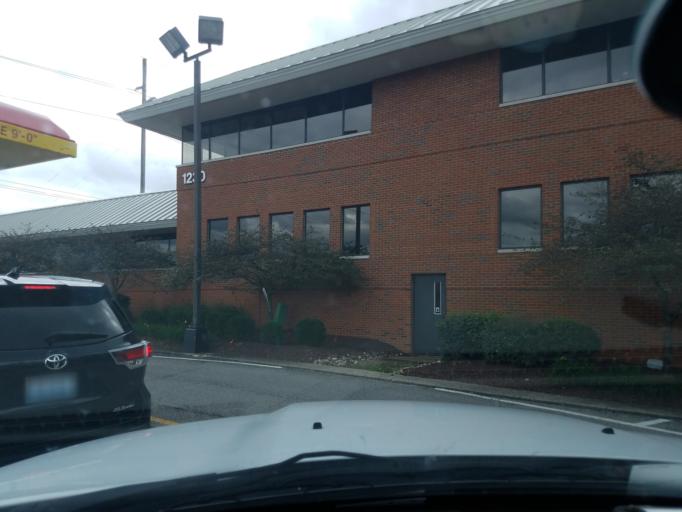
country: US
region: Kentucky
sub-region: Jefferson County
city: Hurstbourne Acres
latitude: 38.2281
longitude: -85.5784
